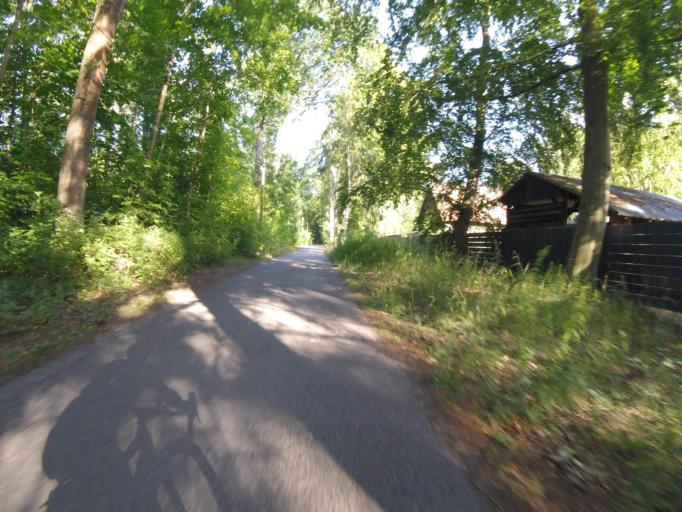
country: DE
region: Brandenburg
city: Erkner
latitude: 52.3306
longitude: 13.7330
